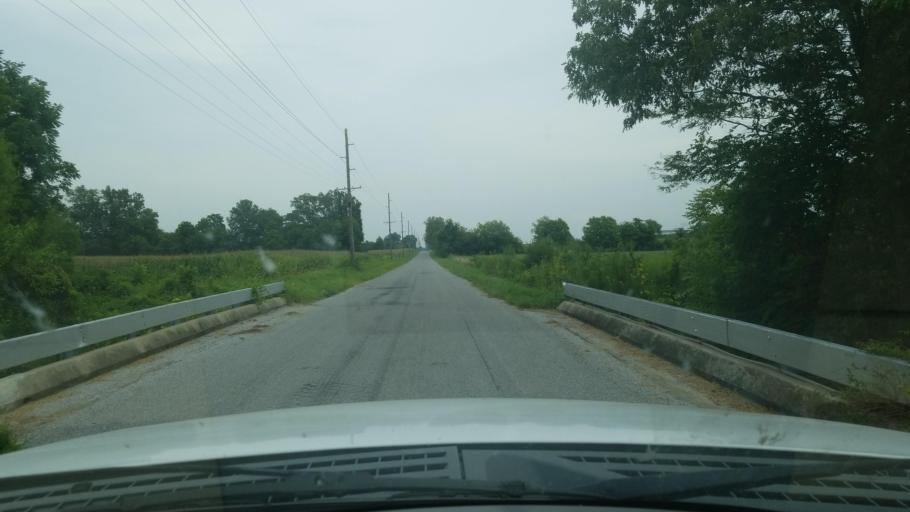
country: US
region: Illinois
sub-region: Saline County
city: Eldorado
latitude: 37.8630
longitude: -88.5188
